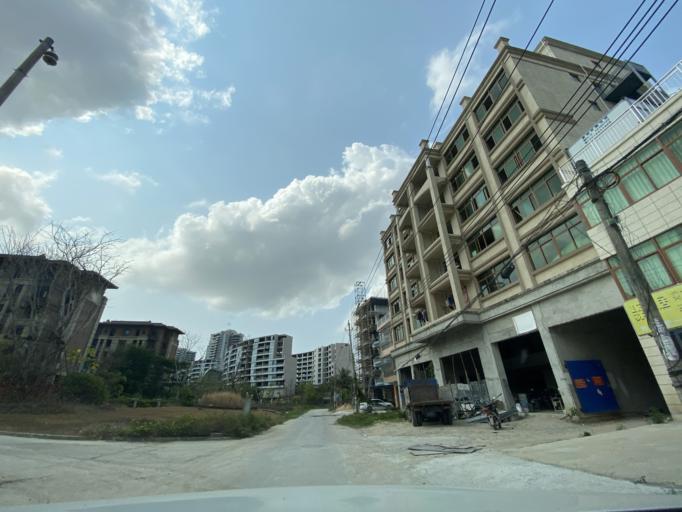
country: CN
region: Hainan
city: Yingzhou
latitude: 18.4178
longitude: 109.8490
